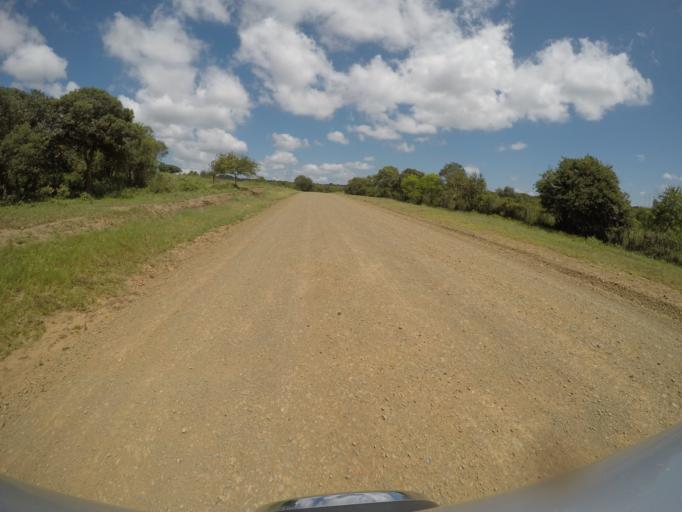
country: ZA
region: KwaZulu-Natal
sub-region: uThungulu District Municipality
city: Empangeni
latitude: -28.5969
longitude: 31.8297
